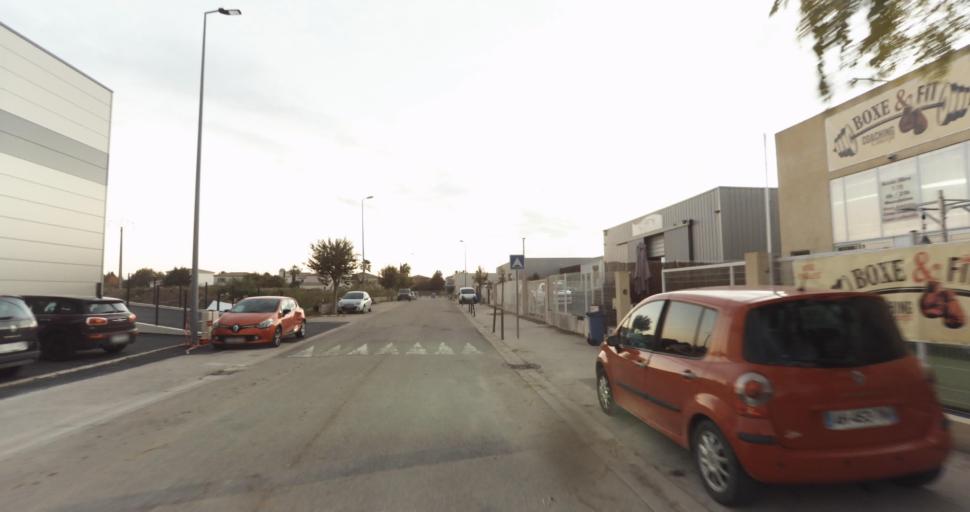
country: FR
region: Languedoc-Roussillon
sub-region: Departement du Gard
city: Aigues-Mortes
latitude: 43.5780
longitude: 4.1907
